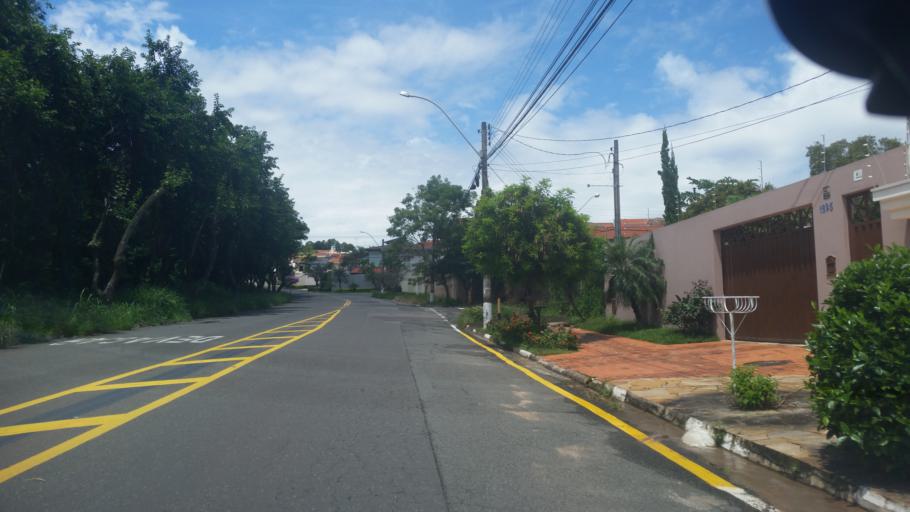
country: BR
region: Sao Paulo
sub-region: Campinas
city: Campinas
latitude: -22.8605
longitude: -47.0586
